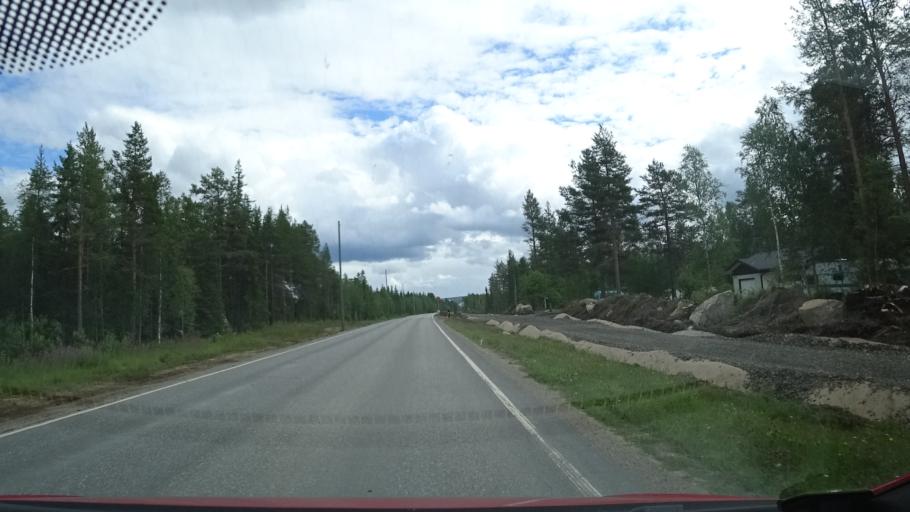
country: FI
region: Lapland
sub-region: Rovaniemi
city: Rovaniemi
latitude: 66.5370
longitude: 25.7256
